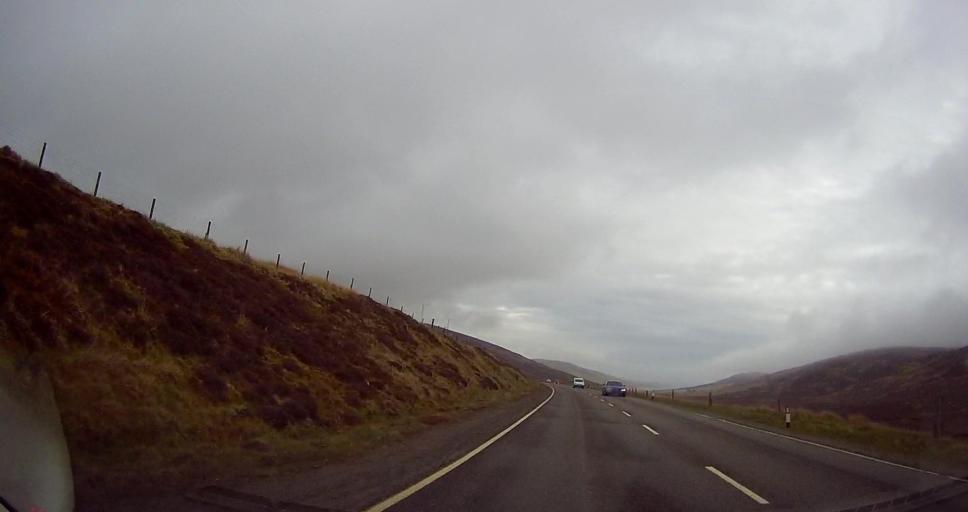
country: GB
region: Scotland
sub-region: Shetland Islands
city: Lerwick
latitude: 60.1477
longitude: -1.2394
